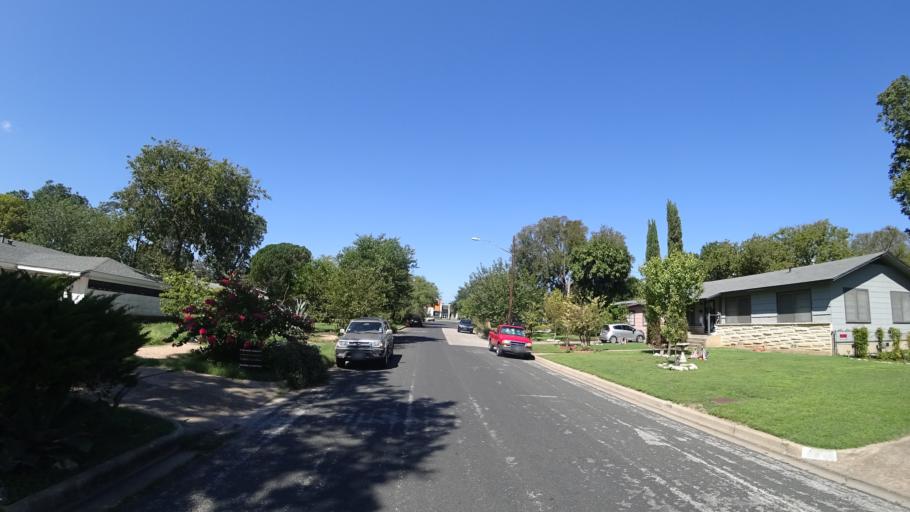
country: US
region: Texas
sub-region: Travis County
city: Austin
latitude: 30.3129
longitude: -97.7033
